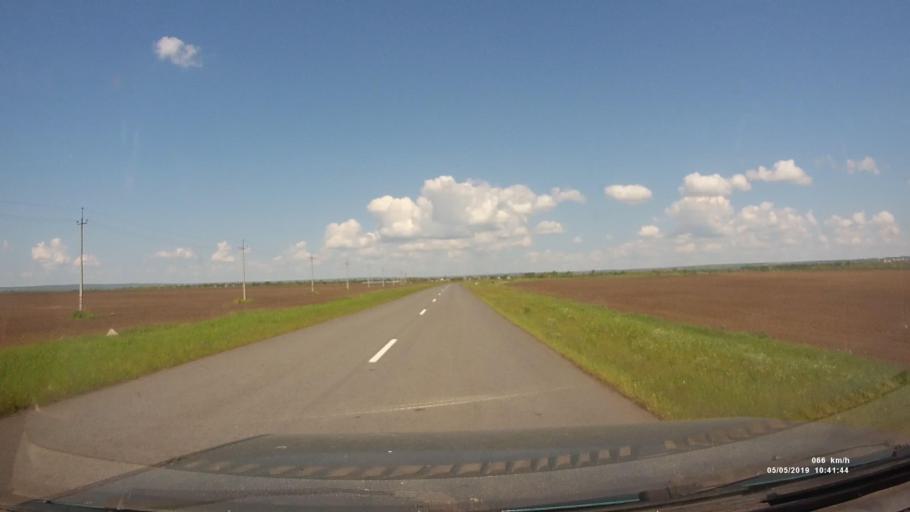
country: RU
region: Rostov
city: Ust'-Donetskiy
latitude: 47.5931
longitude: 40.8396
